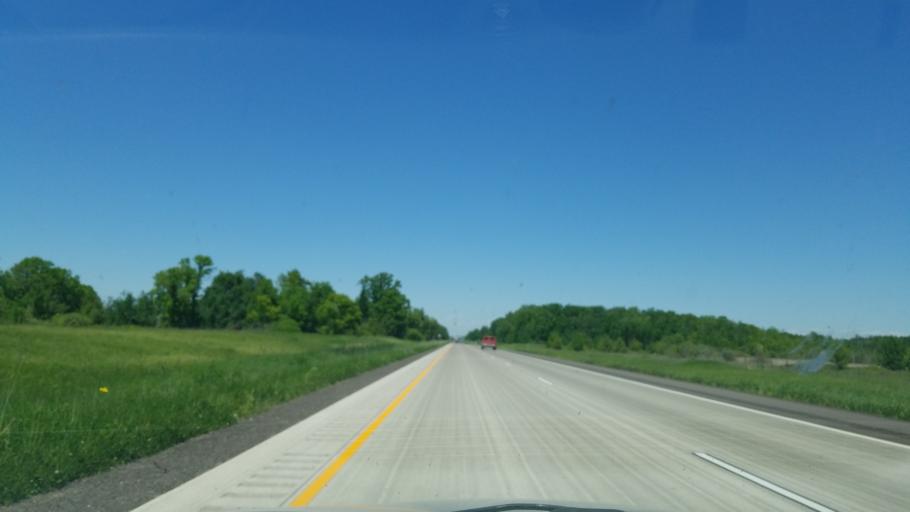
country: US
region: Minnesota
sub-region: Pine County
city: Pine City
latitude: 45.8725
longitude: -92.9696
